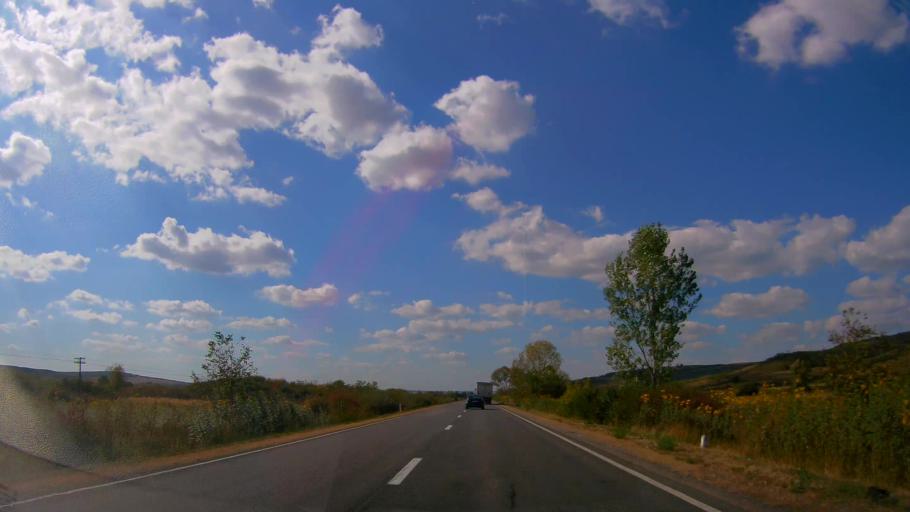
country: RO
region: Salaj
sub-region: Comuna Bocsa
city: Bocsa
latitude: 47.3217
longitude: 22.8907
